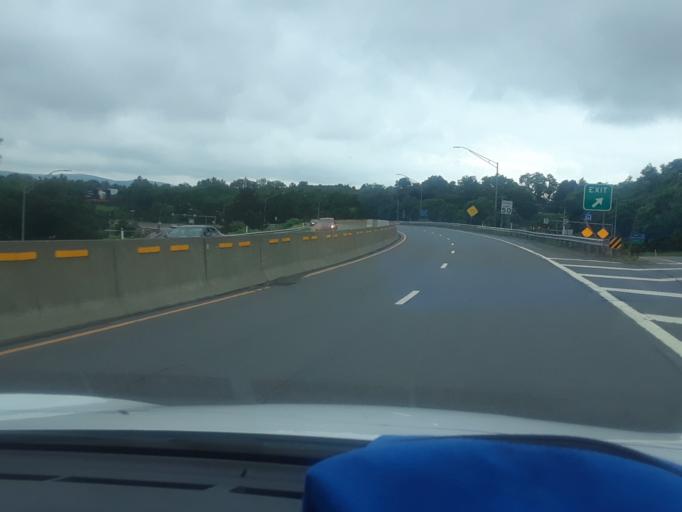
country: US
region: Pennsylvania
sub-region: Lackawanna County
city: Chinchilla
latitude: 41.4462
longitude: -75.6710
